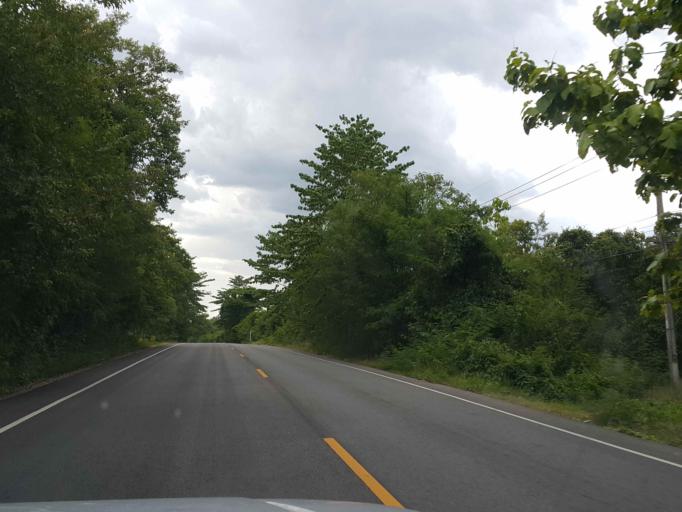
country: TH
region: Lampang
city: Thoen
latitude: 17.6512
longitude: 99.2648
